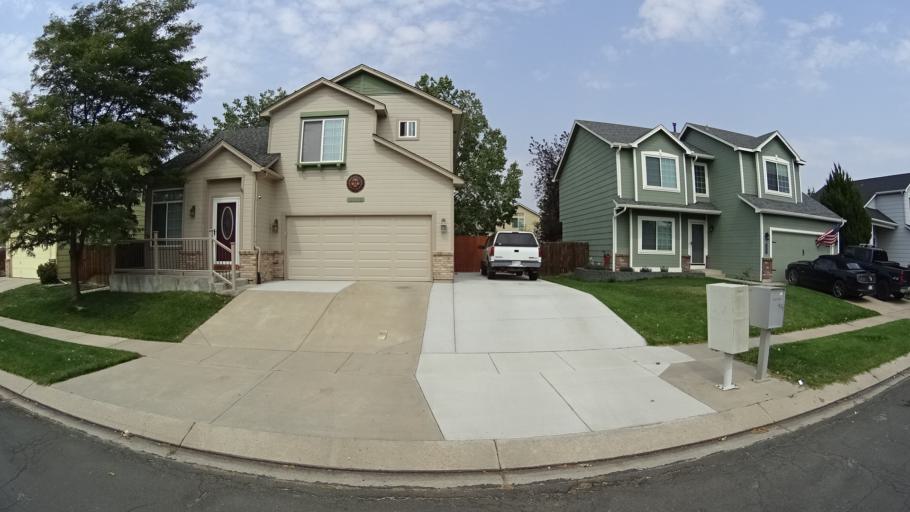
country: US
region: Colorado
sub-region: El Paso County
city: Cimarron Hills
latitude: 38.8232
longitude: -104.7384
